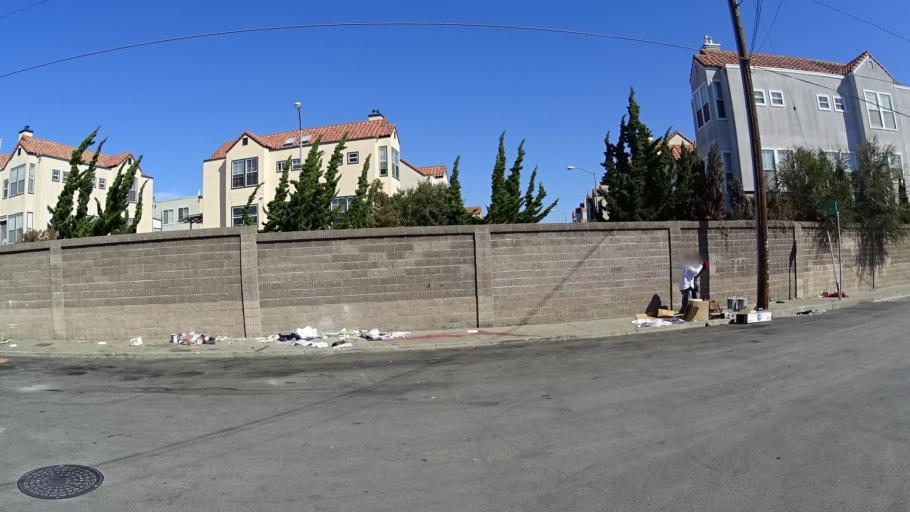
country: US
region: California
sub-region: San Mateo County
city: Brisbane
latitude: 37.7264
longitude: -122.3977
